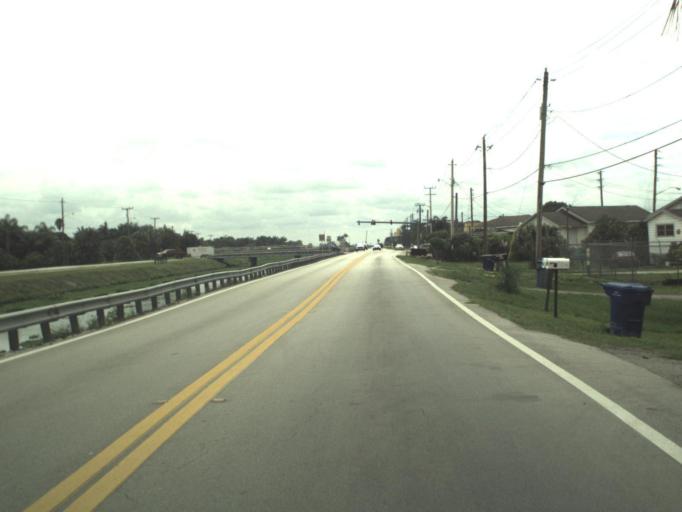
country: US
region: Florida
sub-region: Palm Beach County
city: Belle Glade
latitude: 26.6832
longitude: -80.6619
